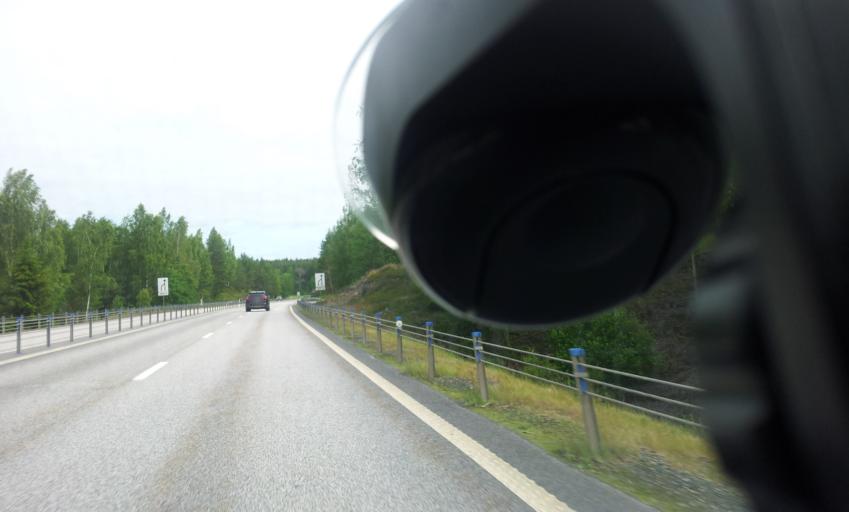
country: SE
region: OEstergoetland
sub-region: Valdemarsviks Kommun
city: Valdemarsvik
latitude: 58.1292
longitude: 16.5326
